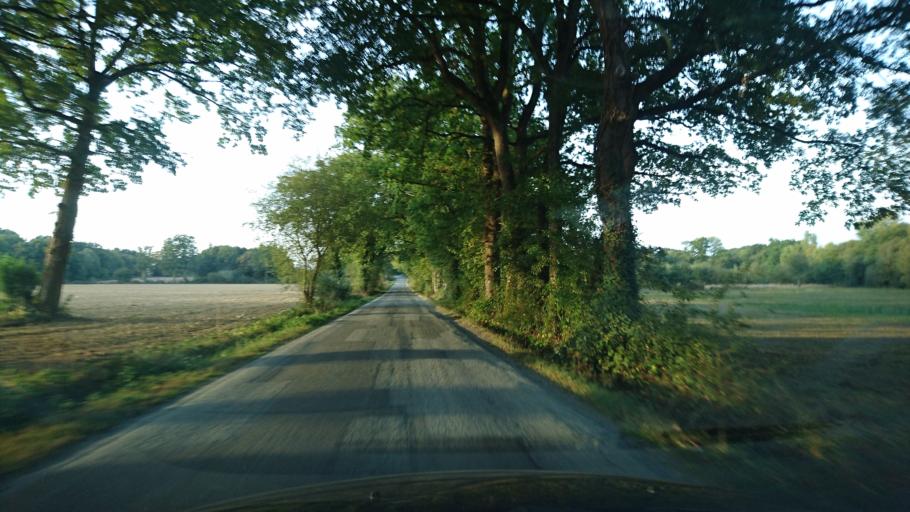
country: FR
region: Brittany
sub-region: Departement d'Ille-et-Vilaine
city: Bains-sur-Oust
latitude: 47.7404
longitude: -2.0509
